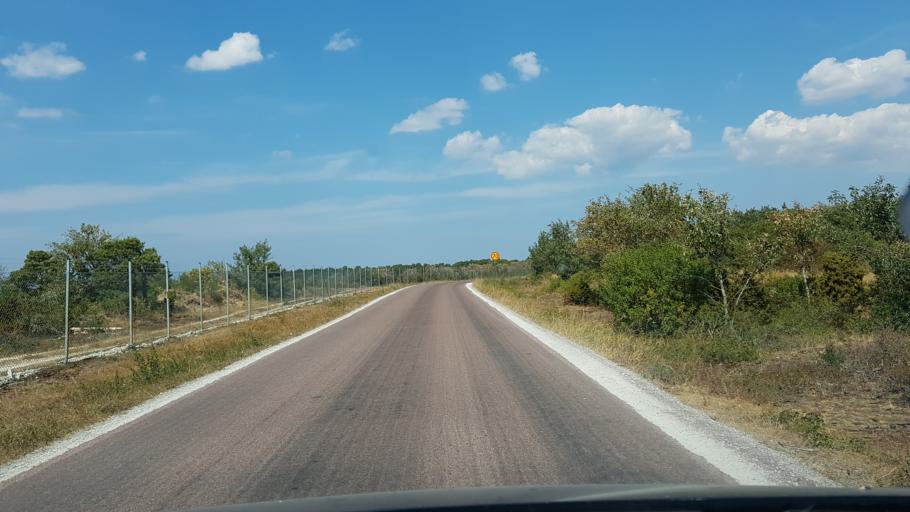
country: SE
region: Gotland
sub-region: Gotland
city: Visby
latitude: 57.6475
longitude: 18.3511
